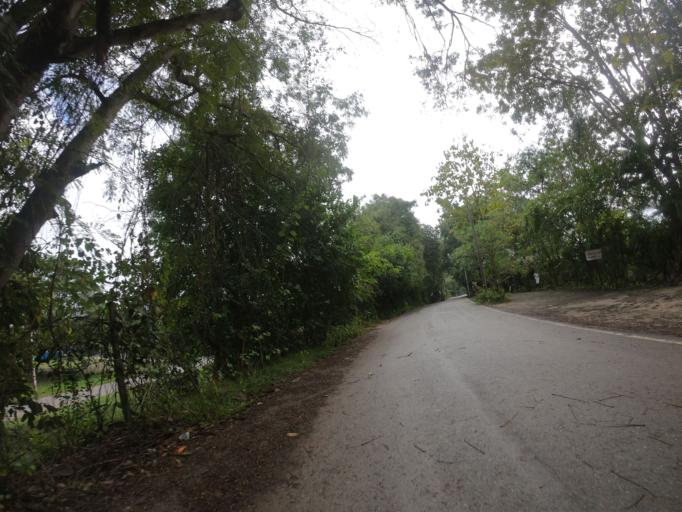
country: TH
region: Chiang Mai
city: Chiang Mai
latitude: 18.8236
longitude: 98.9742
